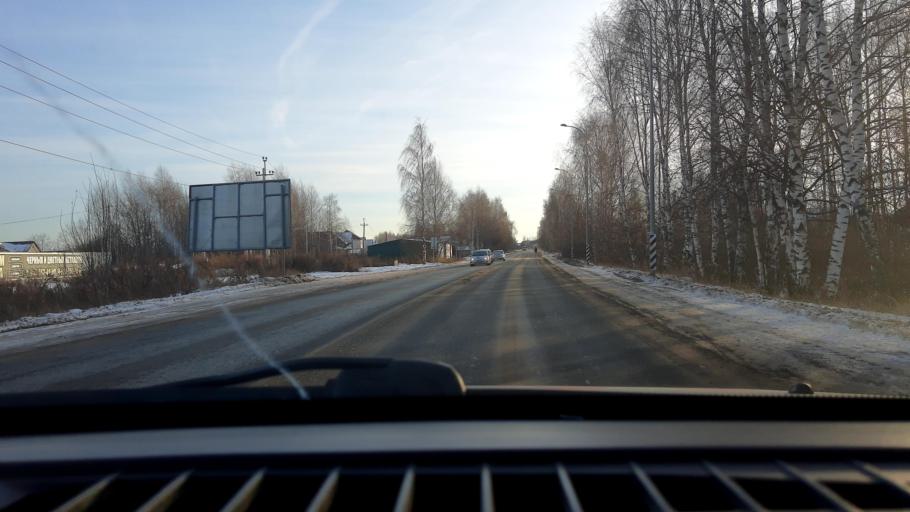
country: RU
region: Nizjnij Novgorod
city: Bor
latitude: 56.3820
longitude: 44.0369
